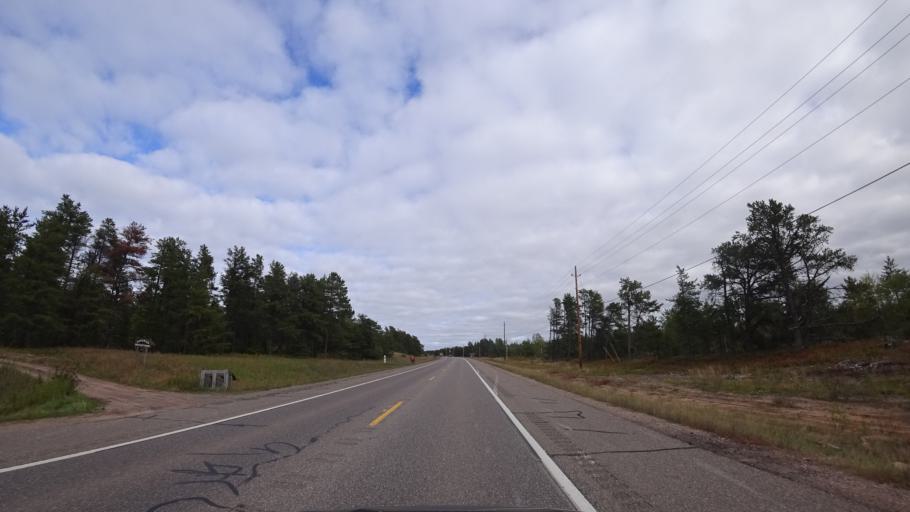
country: US
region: Michigan
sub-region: Marquette County
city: Harvey
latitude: 46.4850
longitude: -87.2549
